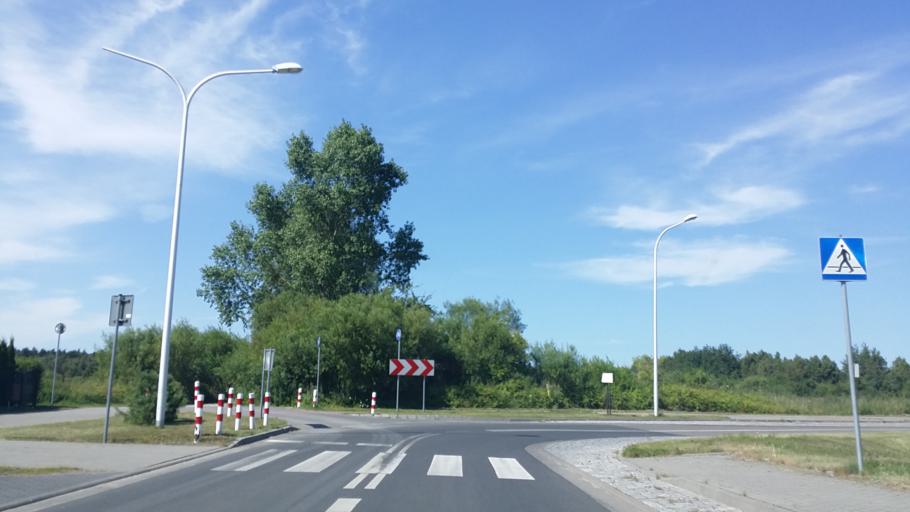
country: PL
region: West Pomeranian Voivodeship
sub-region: Powiat kolobrzeski
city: Grzybowo
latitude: 54.1650
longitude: 15.5168
